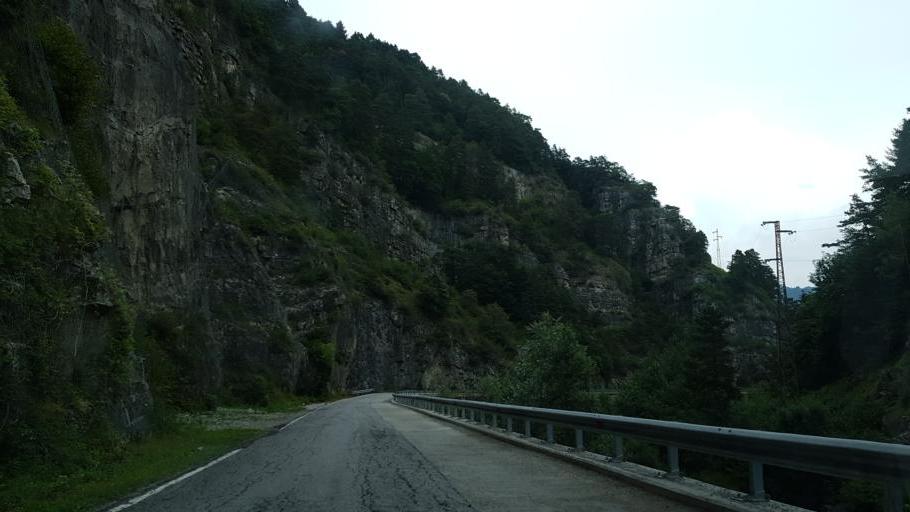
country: IT
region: Piedmont
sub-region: Provincia di Cuneo
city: Stroppo
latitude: 44.4959
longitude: 7.1038
